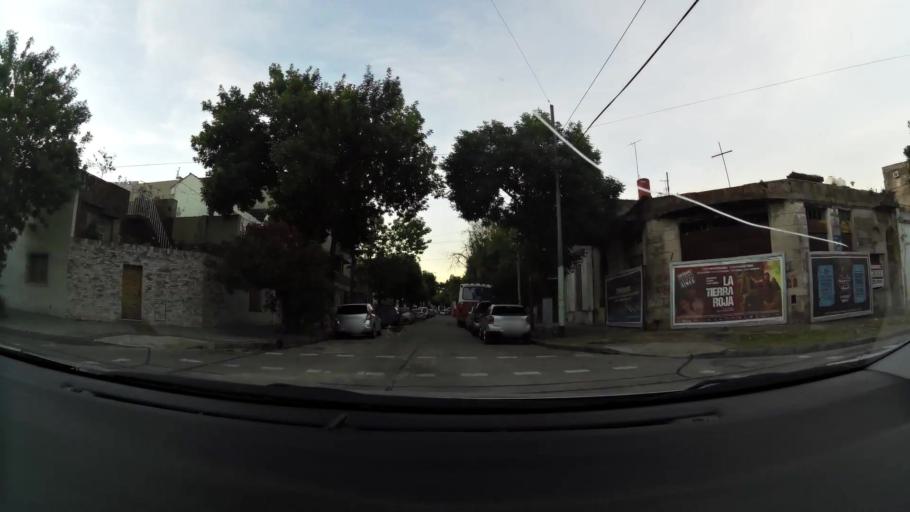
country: AR
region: Buenos Aires F.D.
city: Villa Santa Rita
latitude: -34.6405
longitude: -58.4430
